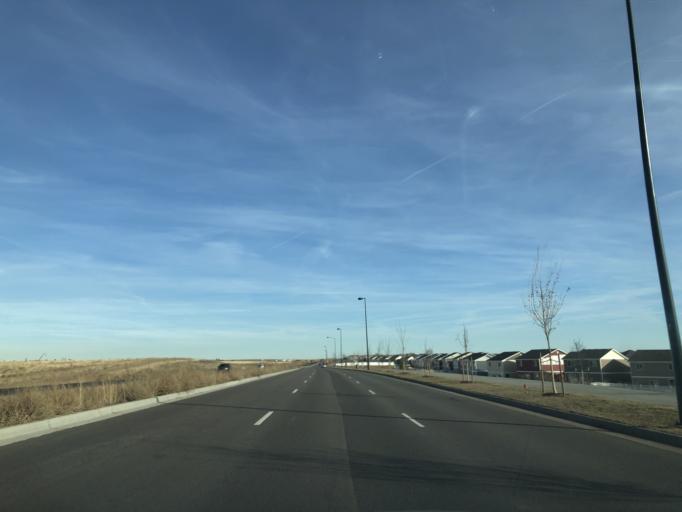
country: US
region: Colorado
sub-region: Adams County
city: Aurora
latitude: 39.7983
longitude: -104.7492
